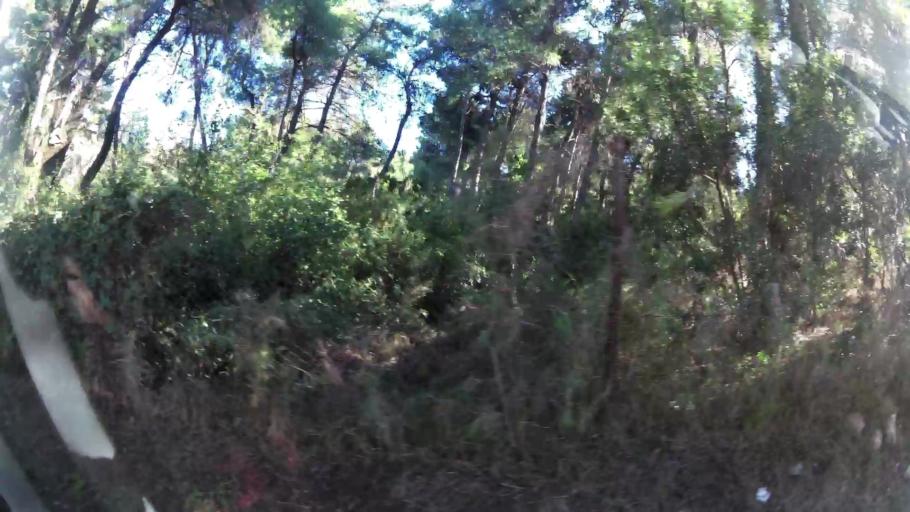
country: GR
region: Attica
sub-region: Nomarchia Anatolikis Attikis
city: Anoixi
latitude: 38.1264
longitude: 23.8481
